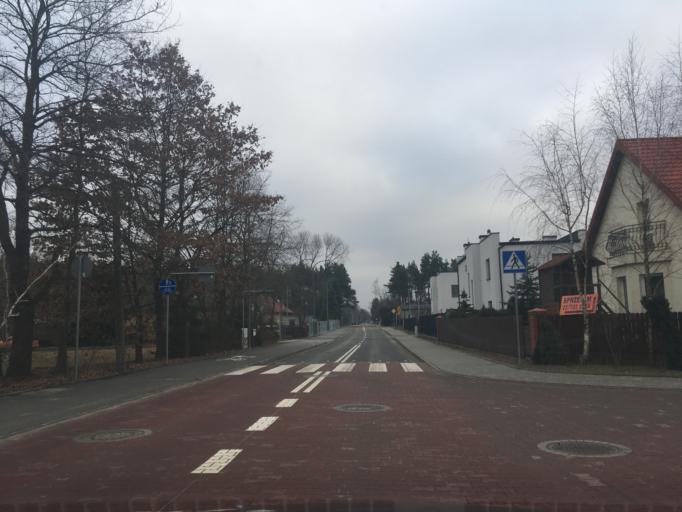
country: PL
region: Masovian Voivodeship
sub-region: Powiat piaseczynski
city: Lesznowola
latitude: 52.0637
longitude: 20.9763
